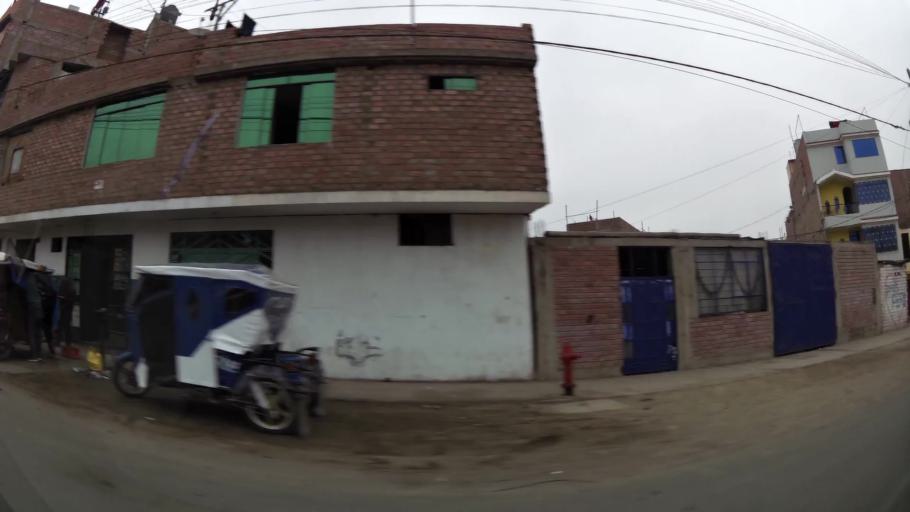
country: PE
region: Lima
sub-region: Lima
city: Urb. Santo Domingo
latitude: -11.8978
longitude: -77.0436
